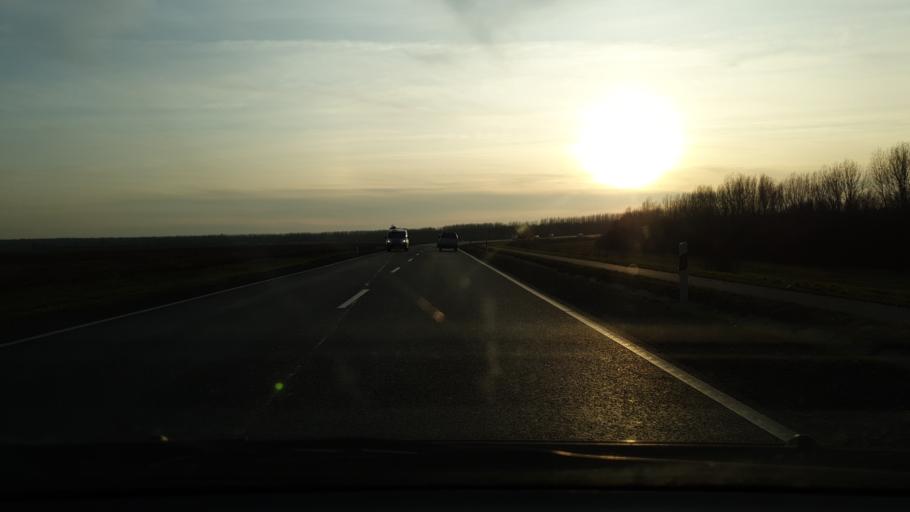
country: HU
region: Jasz-Nagykun-Szolnok
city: Szolnok
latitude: 47.1474
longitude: 20.1887
